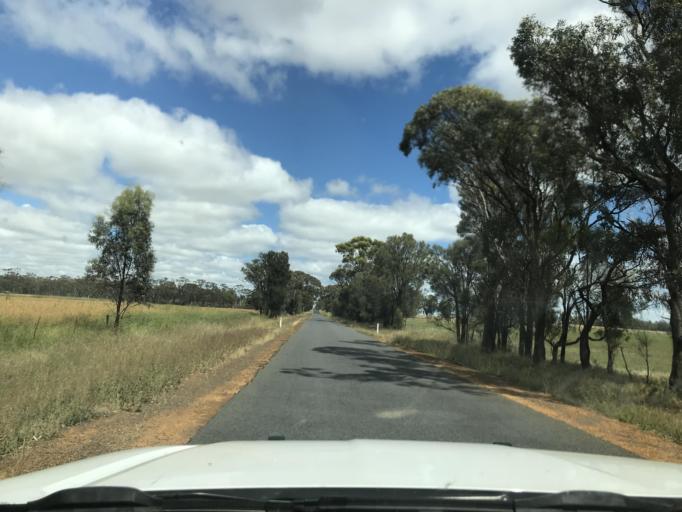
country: AU
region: South Australia
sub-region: Naracoorte and Lucindale
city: Naracoorte
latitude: -36.6831
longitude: 141.3099
